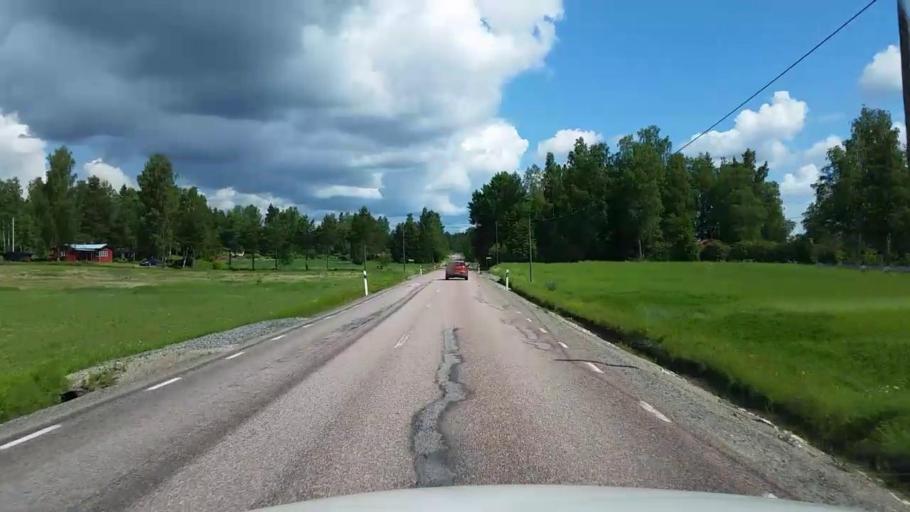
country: SE
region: Vaestmanland
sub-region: Skinnskattebergs Kommun
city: Skinnskatteberg
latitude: 59.7465
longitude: 15.8109
